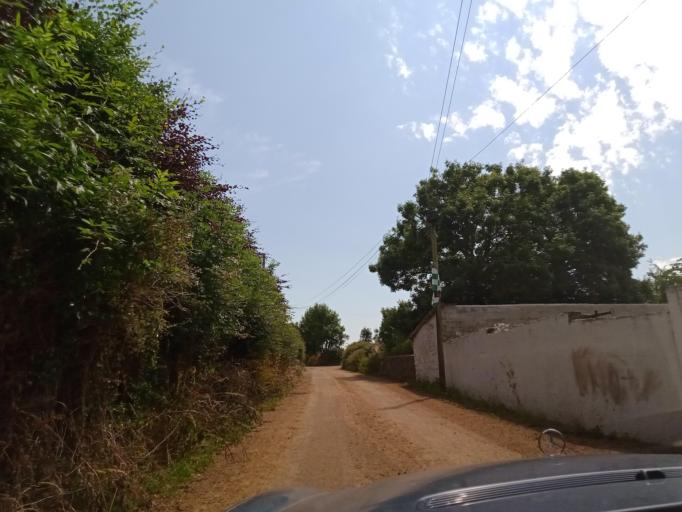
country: IE
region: Leinster
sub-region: Kilkenny
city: Mooncoin
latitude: 52.2689
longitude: -7.2274
